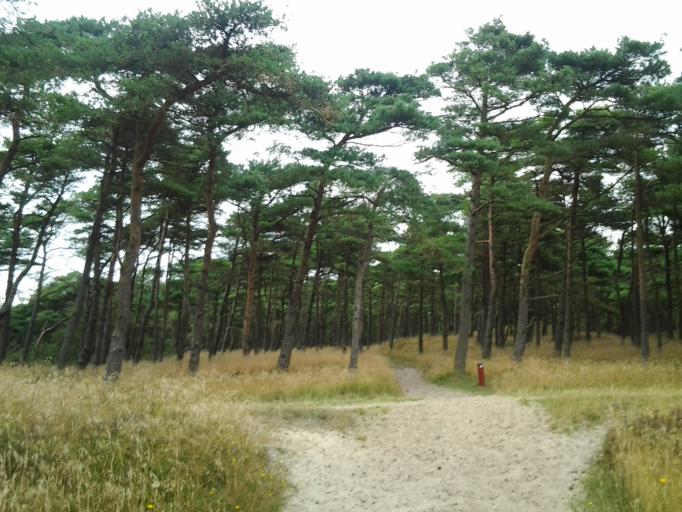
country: DE
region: Schleswig-Holstein
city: List
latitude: 55.1165
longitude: 8.5281
